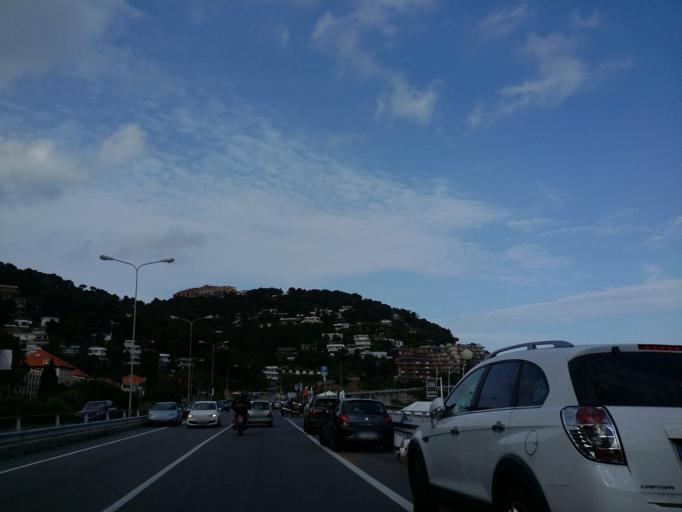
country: IT
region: Liguria
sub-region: Provincia di Savona
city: Bergeggi
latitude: 44.2364
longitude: 8.4340
